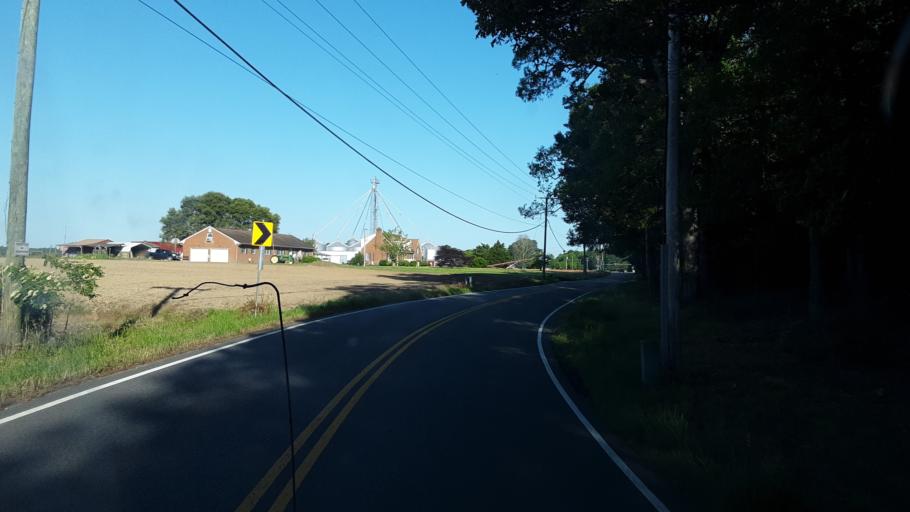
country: US
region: Virginia
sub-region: City of Virginia Beach
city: Virginia Beach
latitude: 36.7202
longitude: -76.0449
